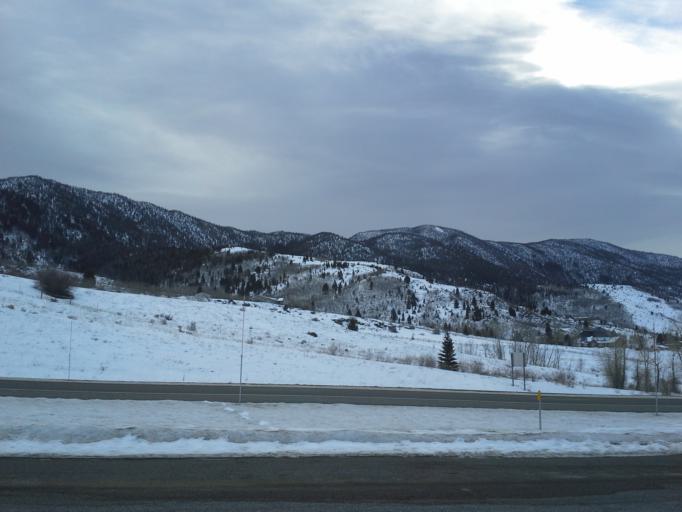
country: US
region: Montana
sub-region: Silver Bow County
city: Butte
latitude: 45.9912
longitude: -112.4752
